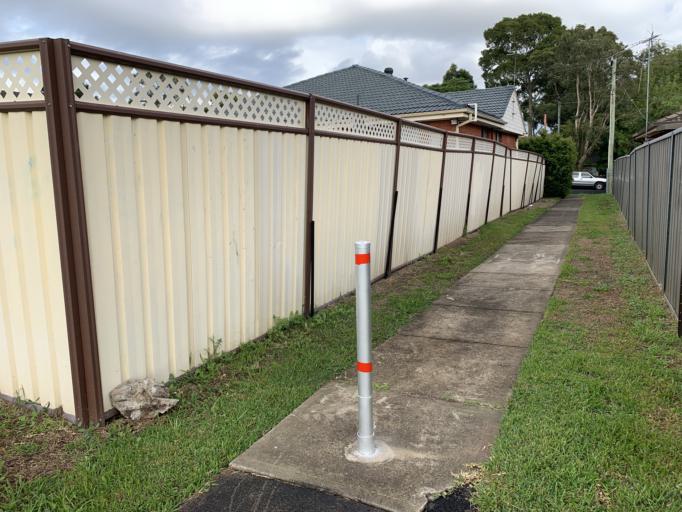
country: AU
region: New South Wales
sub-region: Holroyd
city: Girraween
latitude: -33.7908
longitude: 150.9209
